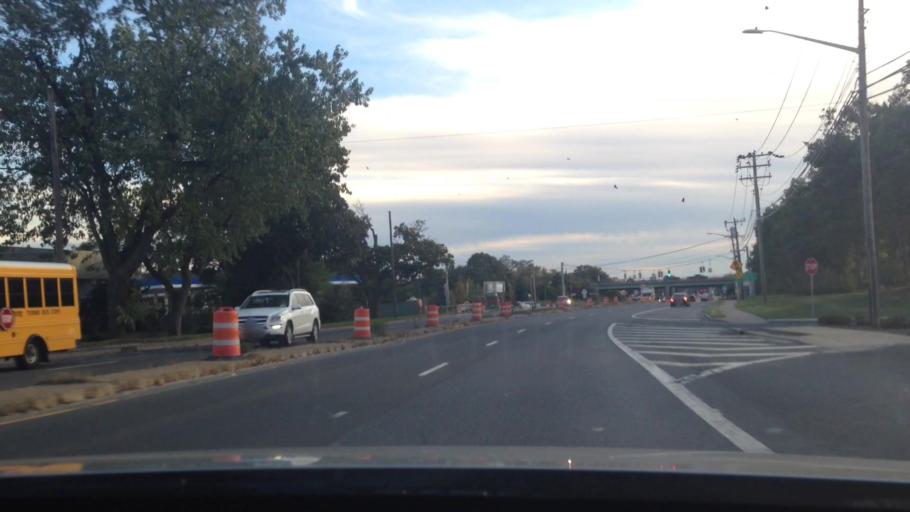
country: US
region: New York
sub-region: Suffolk County
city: Medford
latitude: 40.8262
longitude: -72.9954
